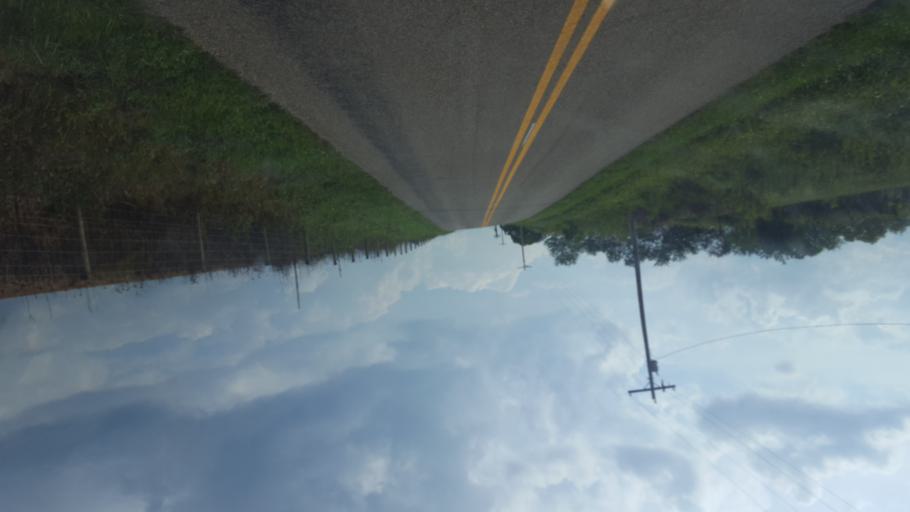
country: US
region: Ohio
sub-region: Knox County
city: Gambier
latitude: 40.3355
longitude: -82.3855
